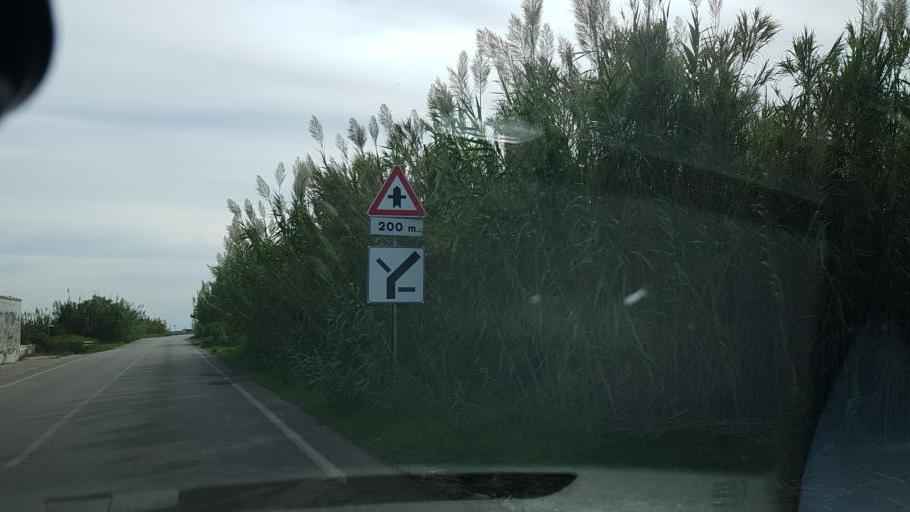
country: IT
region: Apulia
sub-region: Provincia di Lecce
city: Borgagne
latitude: 40.2966
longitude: 18.4121
